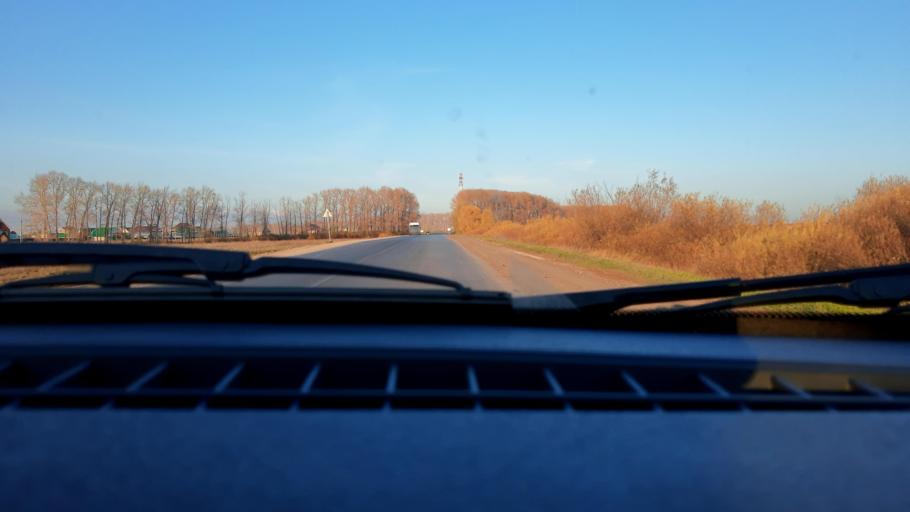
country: RU
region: Bashkortostan
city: Asanovo
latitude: 54.8132
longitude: 55.5822
